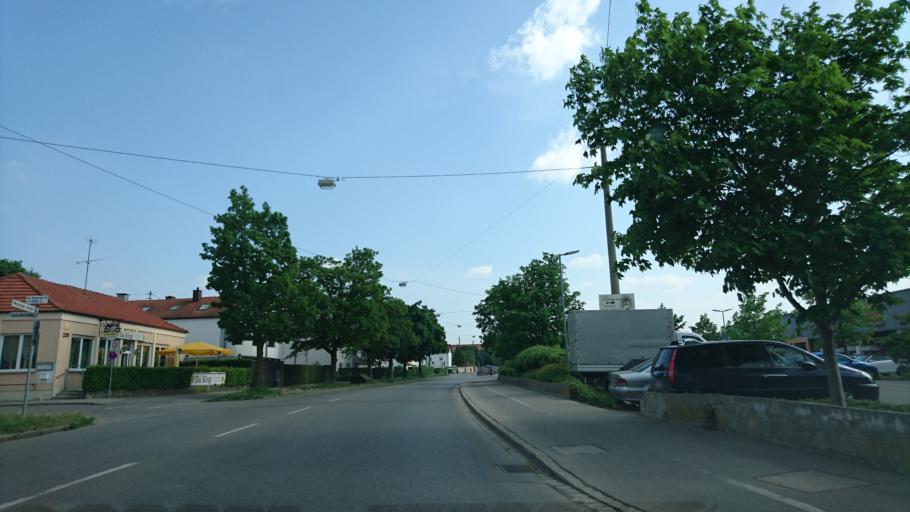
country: DE
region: Bavaria
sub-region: Swabia
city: Augsburg
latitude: 48.3981
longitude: 10.9148
